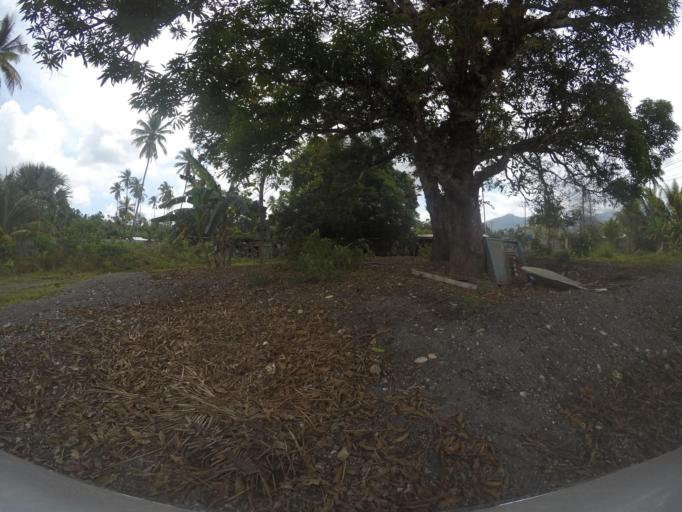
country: TL
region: Viqueque
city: Viqueque
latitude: -8.8407
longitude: 126.3698
